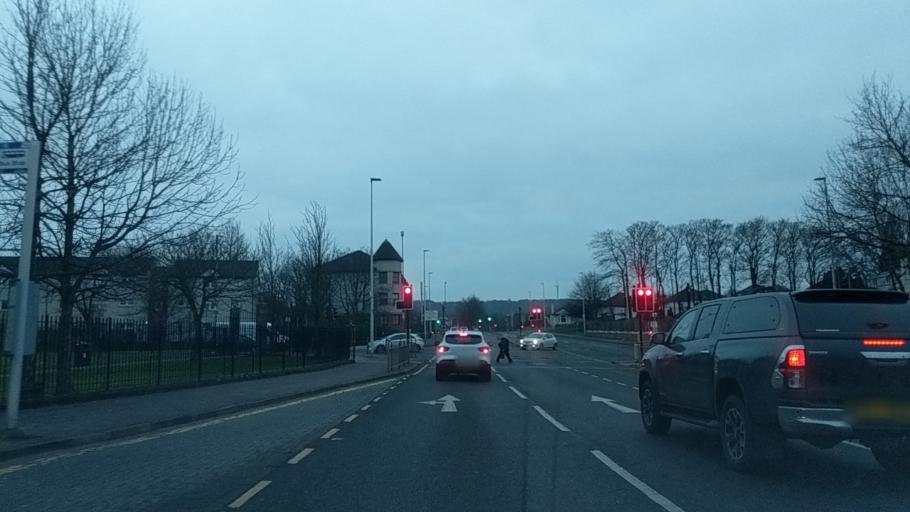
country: GB
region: Scotland
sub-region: South Lanarkshire
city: Rutherglen
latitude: 55.8209
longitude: -4.2156
